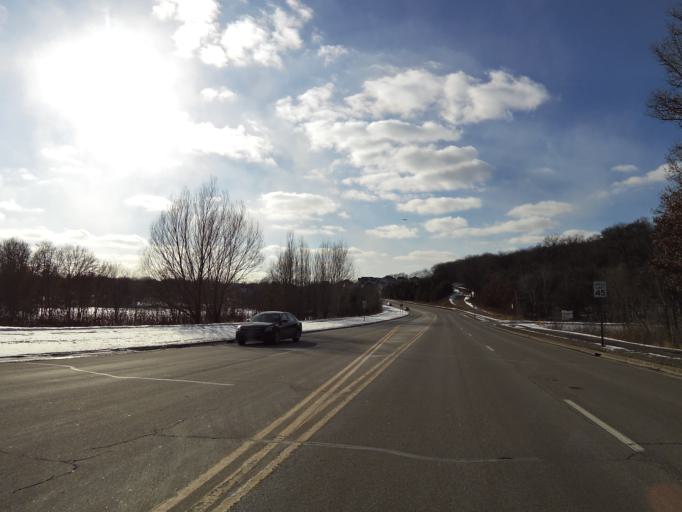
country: US
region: Minnesota
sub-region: Dakota County
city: Eagan
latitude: 44.7681
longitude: -93.1678
